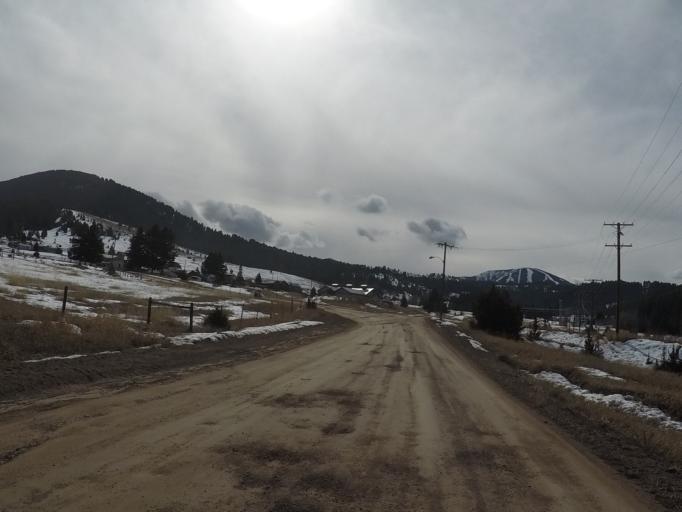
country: US
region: Montana
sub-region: Granite County
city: Philipsburg
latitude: 46.3280
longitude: -113.2933
